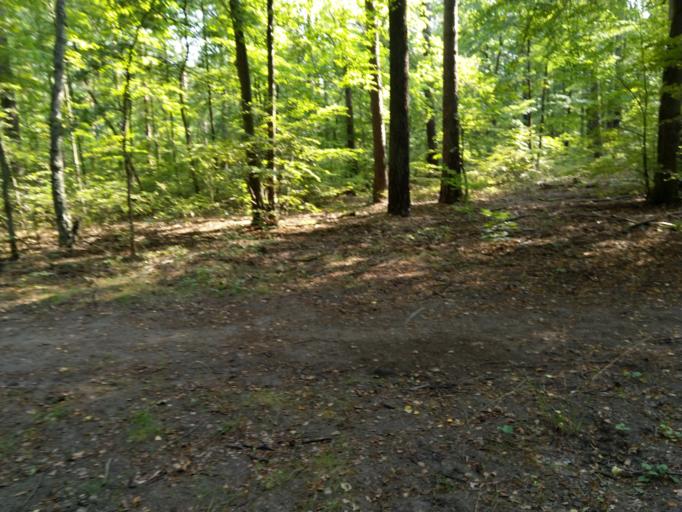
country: DE
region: Berlin
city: Rahnsdorf
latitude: 52.4517
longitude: 13.7195
